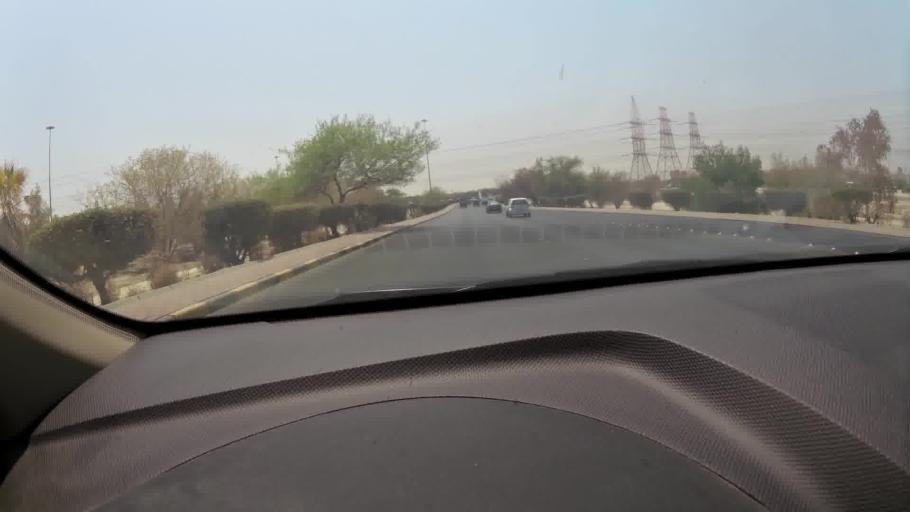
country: KW
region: Mubarak al Kabir
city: Sabah as Salim
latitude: 29.2659
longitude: 48.0395
